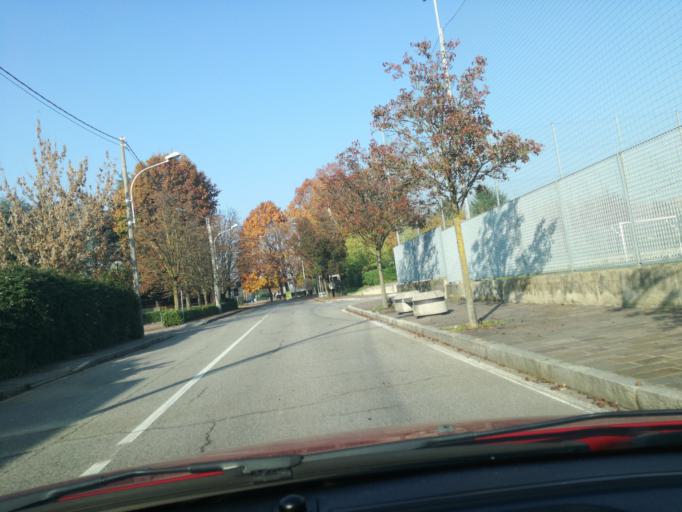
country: IT
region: Lombardy
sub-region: Provincia di Monza e Brianza
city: Cavenago di Brianza
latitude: 45.5881
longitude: 9.4155
